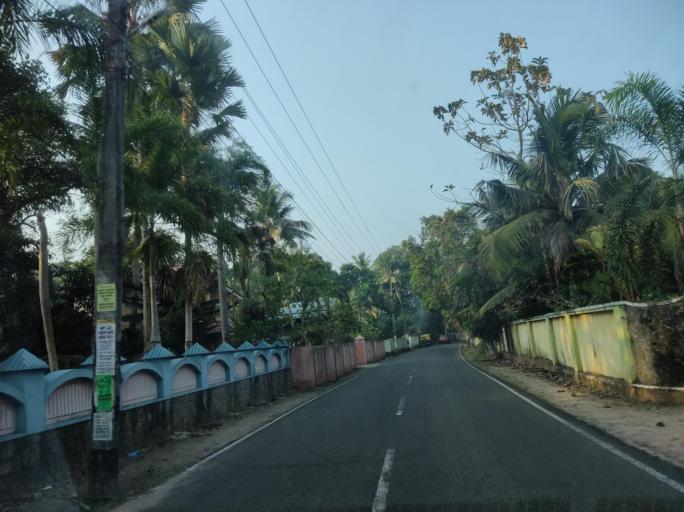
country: IN
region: Kerala
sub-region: Alappuzha
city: Shertallai
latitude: 9.6111
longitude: 76.3130
